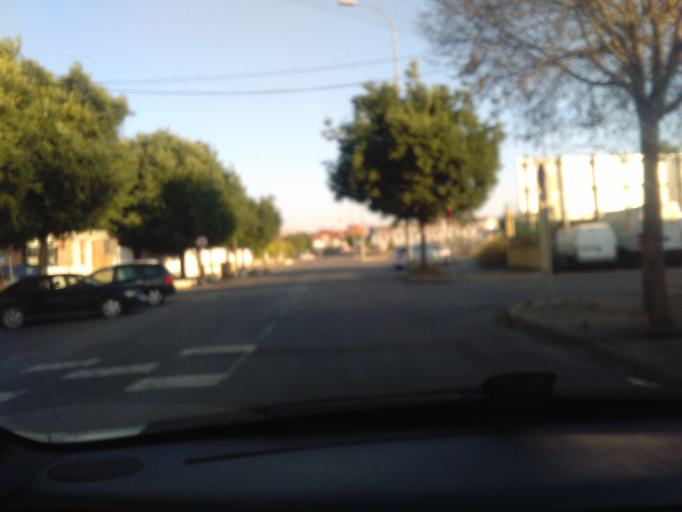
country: ES
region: Andalusia
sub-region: Provincia de Sevilla
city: Sevilla
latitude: 37.3942
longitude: -5.9467
